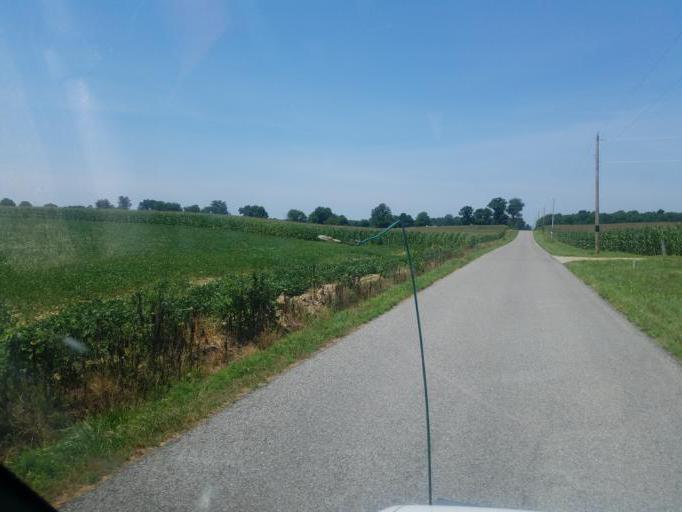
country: US
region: Ohio
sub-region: Logan County
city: West Liberty
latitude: 40.2907
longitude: -83.8058
